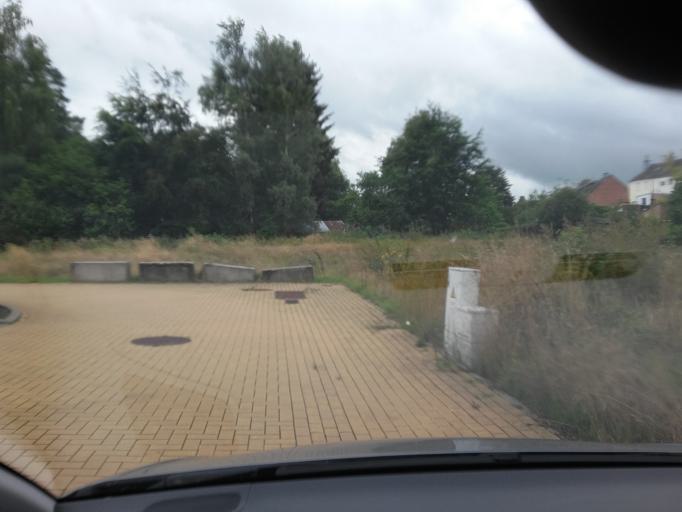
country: BE
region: Wallonia
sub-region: Province du Luxembourg
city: Arlon
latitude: 49.6774
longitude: 5.8054
